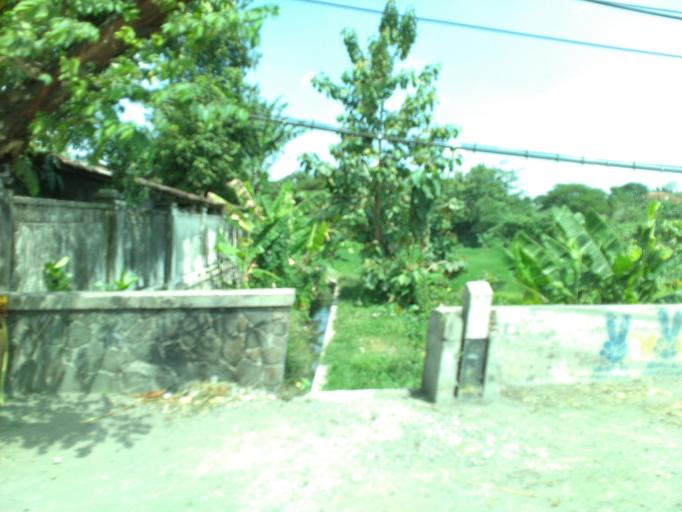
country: ID
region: Central Java
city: Klaten
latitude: -7.7165
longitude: 110.5858
